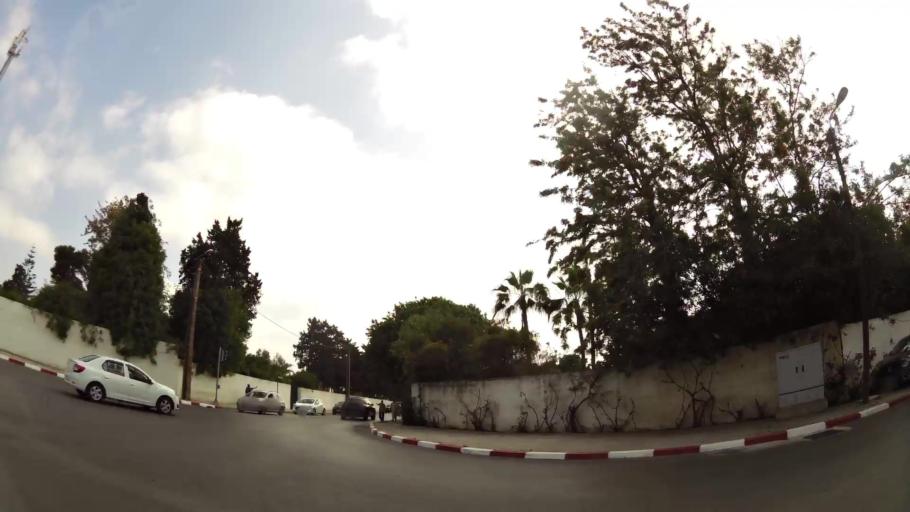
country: MA
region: Rabat-Sale-Zemmour-Zaer
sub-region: Rabat
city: Rabat
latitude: 33.9763
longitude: -6.8480
